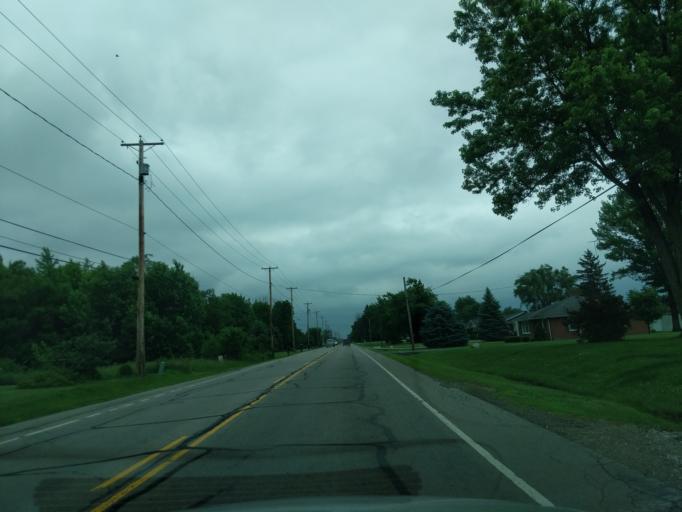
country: US
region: Indiana
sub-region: Madison County
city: Alexandria
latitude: 40.2778
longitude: -85.6658
